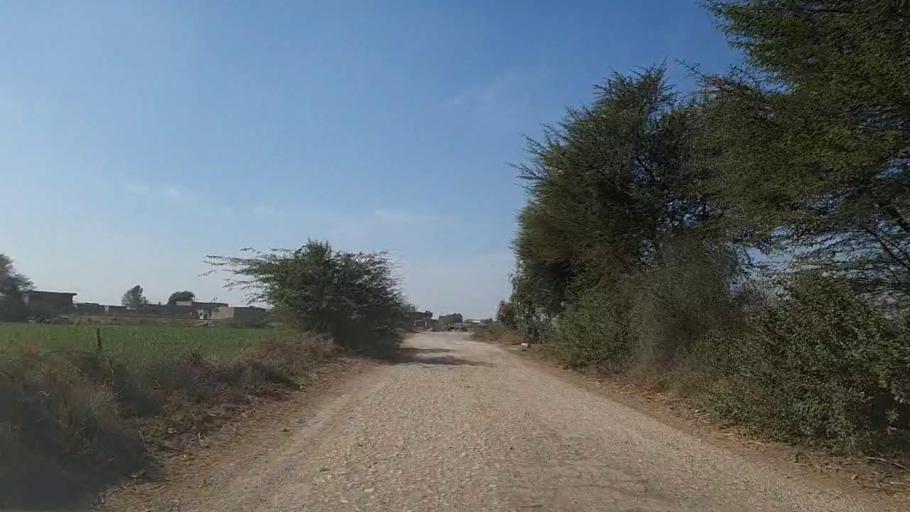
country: PK
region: Sindh
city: Nawabshah
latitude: 26.2239
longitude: 68.4224
